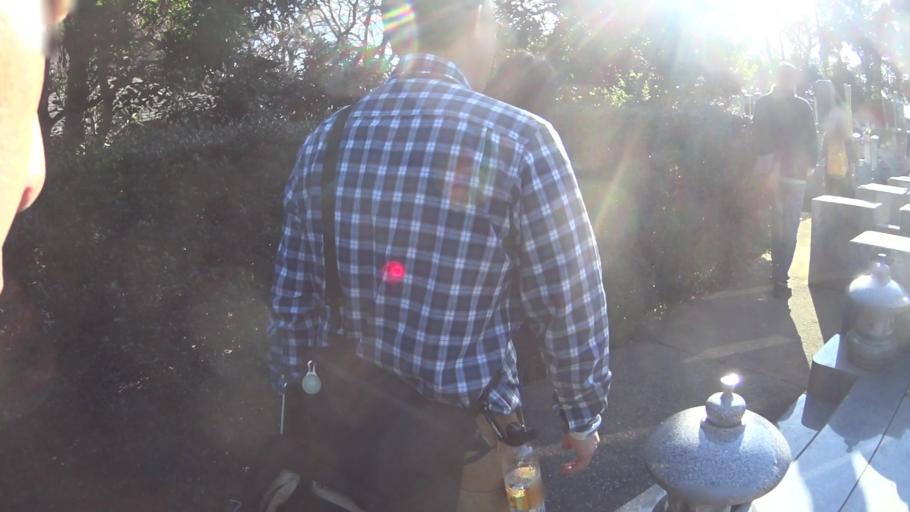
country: JP
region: Saitama
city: Shimotoda
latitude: 35.8417
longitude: 139.6899
